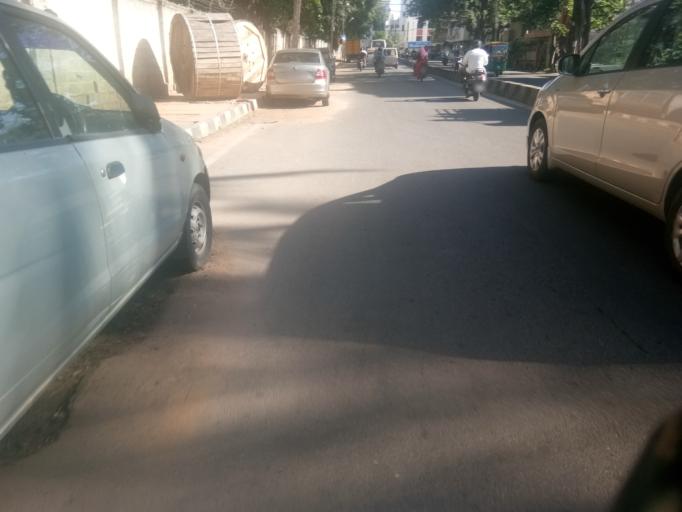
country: IN
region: Karnataka
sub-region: Bangalore Urban
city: Bangalore
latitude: 13.0174
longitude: 77.5982
